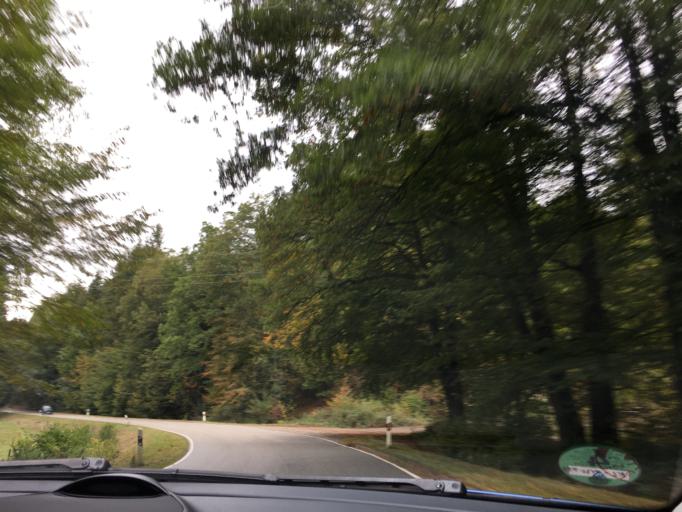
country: DE
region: Rheinland-Pfalz
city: Schmalenberg
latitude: 49.3418
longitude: 7.7422
